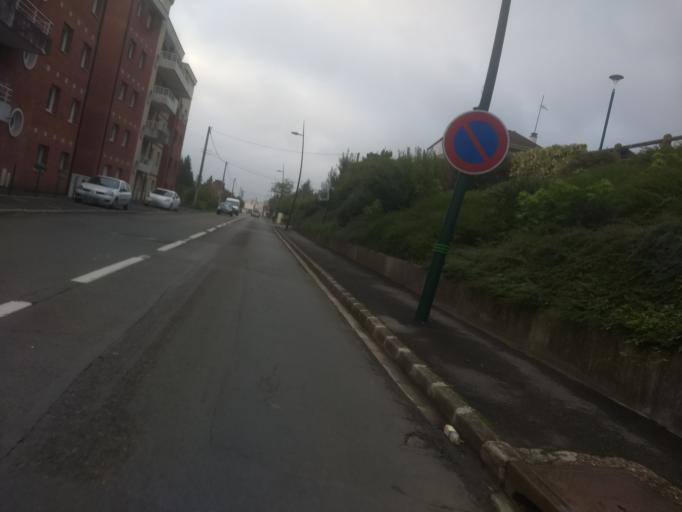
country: FR
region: Nord-Pas-de-Calais
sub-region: Departement du Pas-de-Calais
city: Saint-Laurent-Blangy
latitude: 50.3007
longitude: 2.7957
